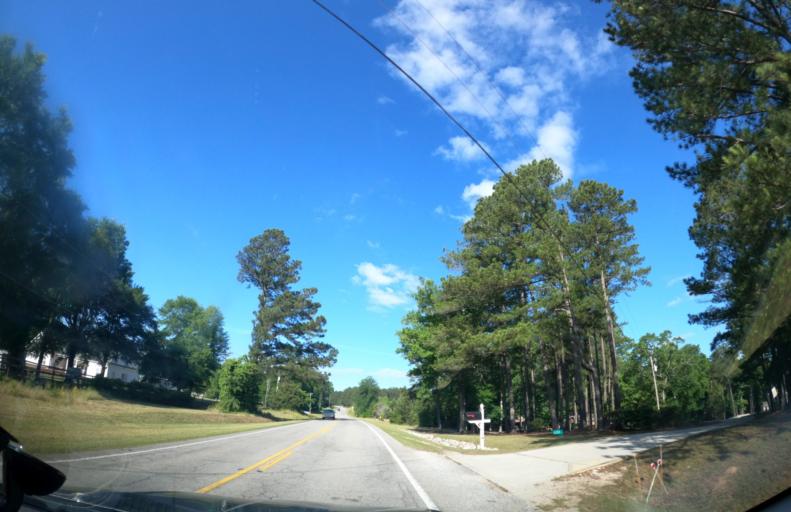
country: US
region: Georgia
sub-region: Columbia County
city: Harlem
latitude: 33.4418
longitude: -82.2678
